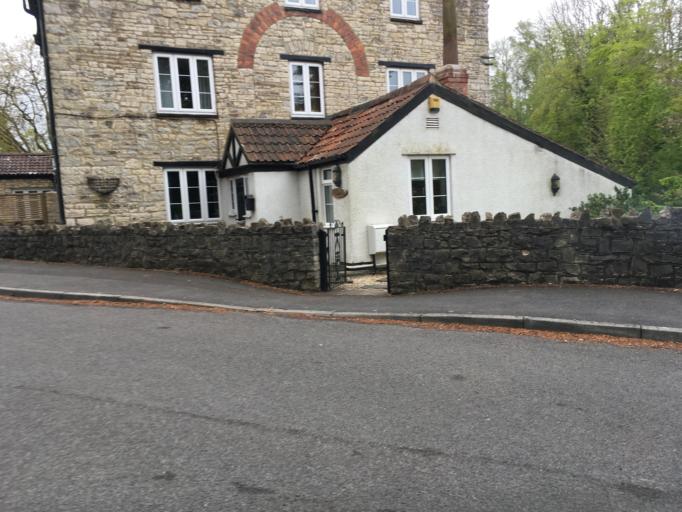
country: GB
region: England
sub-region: Bath and North East Somerset
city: Clutton
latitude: 51.3266
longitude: -2.5177
